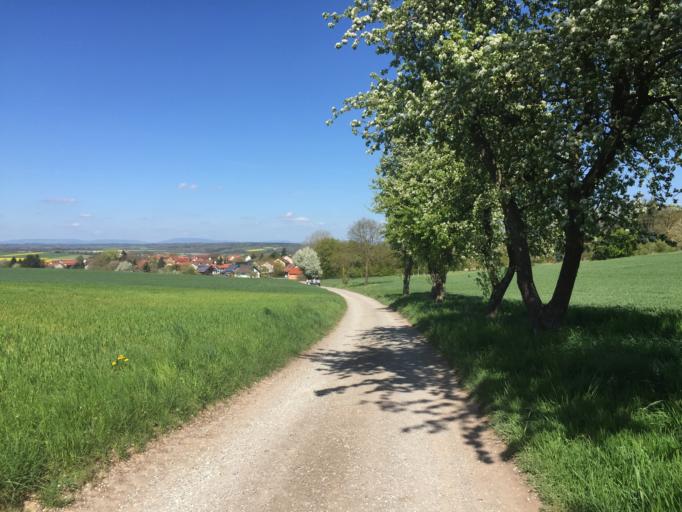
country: DE
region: Bavaria
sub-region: Regierungsbezirk Unterfranken
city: Sulzfeld
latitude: 50.2614
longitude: 10.4156
